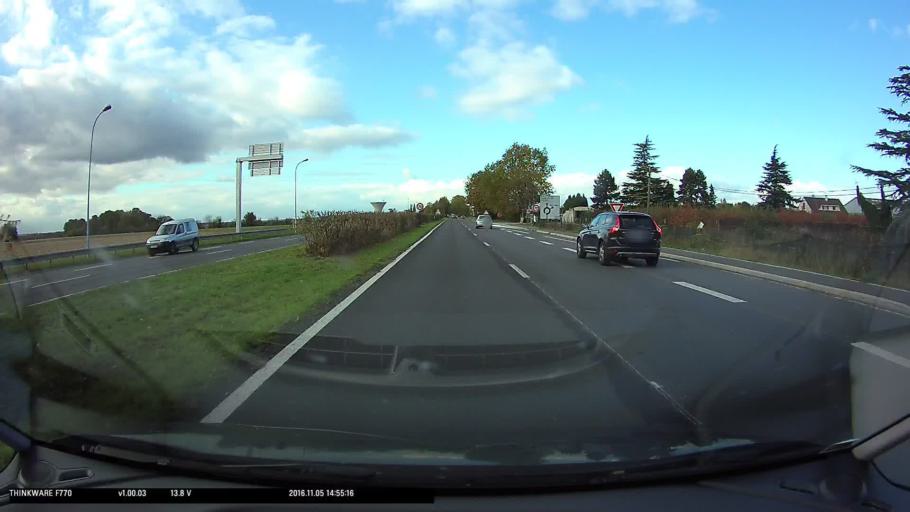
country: FR
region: Ile-de-France
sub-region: Departement du Val-d'Oise
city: Osny
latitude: 49.0775
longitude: 2.0743
